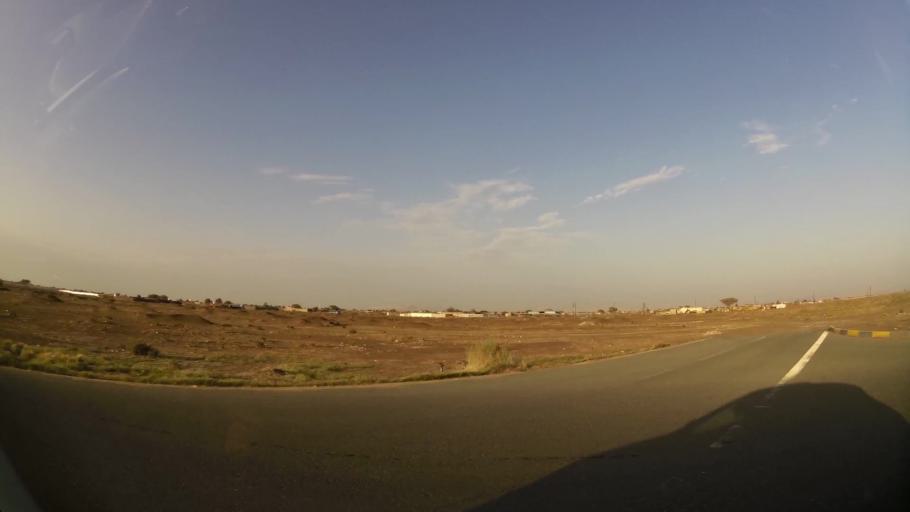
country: AE
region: Abu Dhabi
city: Al Ain
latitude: 24.1557
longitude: 55.8294
